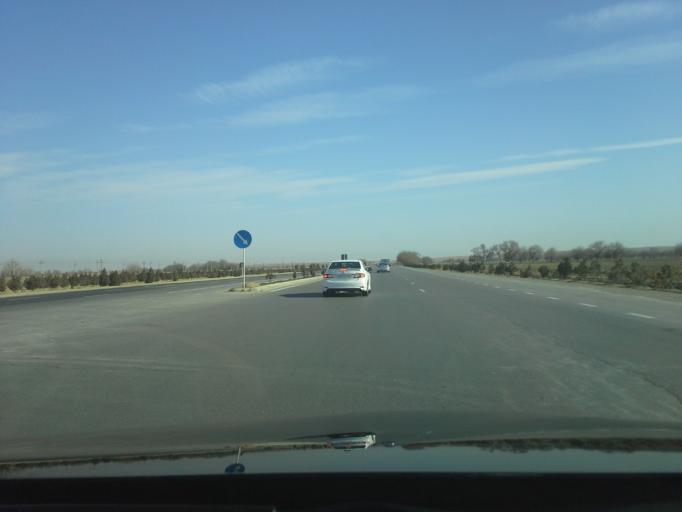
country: TM
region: Ahal
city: Annau
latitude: 37.9020
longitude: 58.5644
